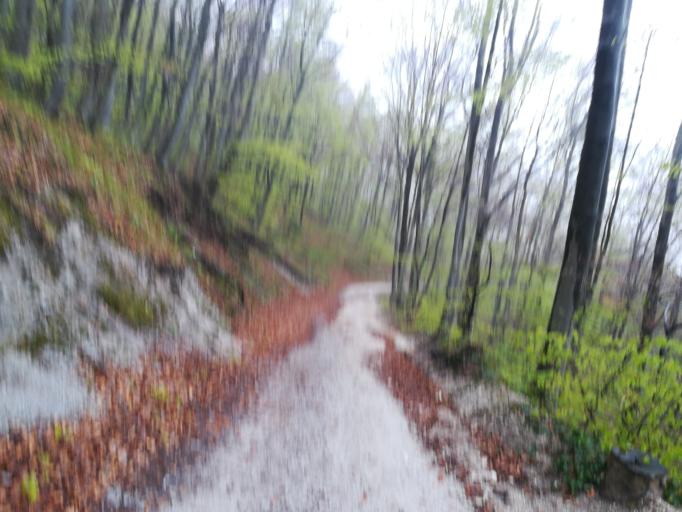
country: HR
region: Varazdinska
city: Ivanec
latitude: 46.1890
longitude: 16.1485
